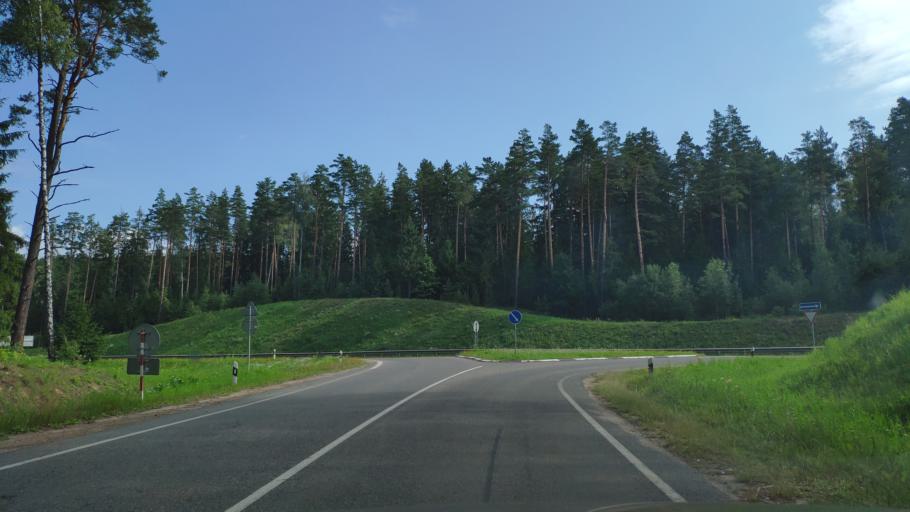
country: BY
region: Minsk
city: Khatsyezhyna
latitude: 53.9601
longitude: 27.3162
